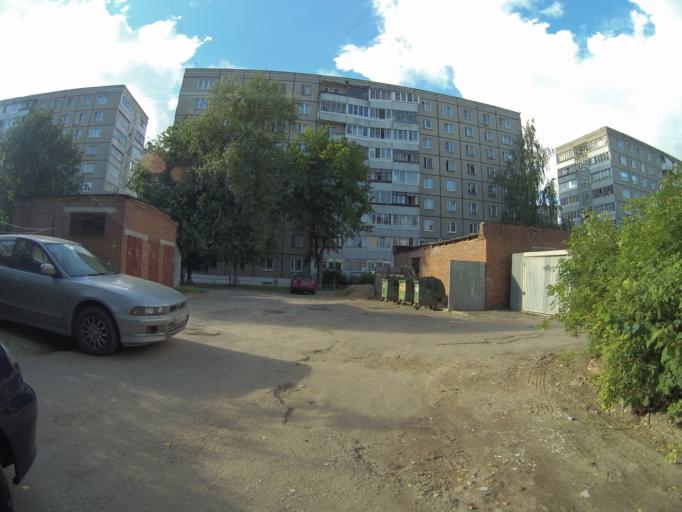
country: RU
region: Vladimir
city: Vladimir
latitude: 56.1492
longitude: 40.4286
